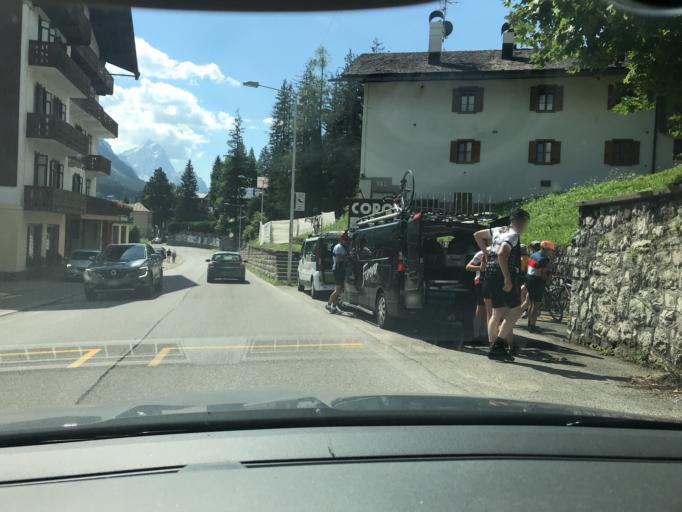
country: IT
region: Veneto
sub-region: Provincia di Belluno
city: Cortina d'Ampezzo
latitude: 46.5401
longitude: 12.1298
